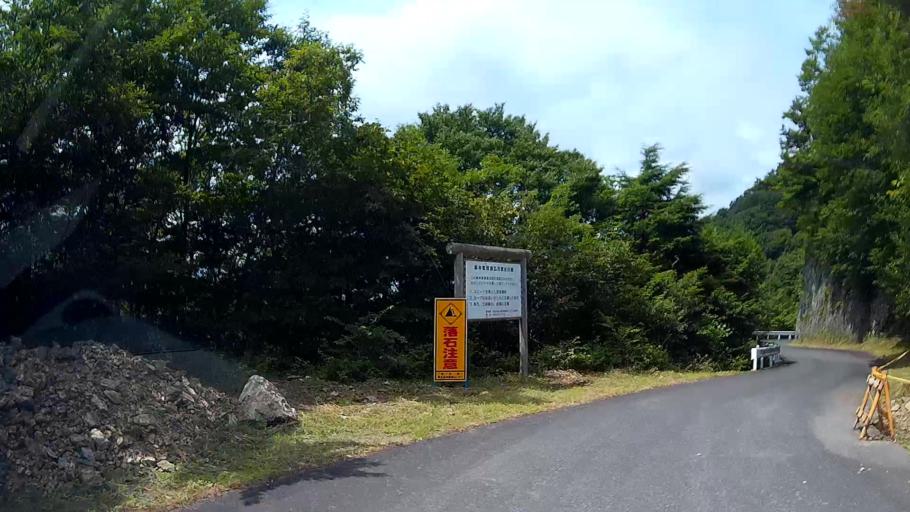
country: JP
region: Saitama
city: Chichibu
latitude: 35.8788
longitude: 139.1096
